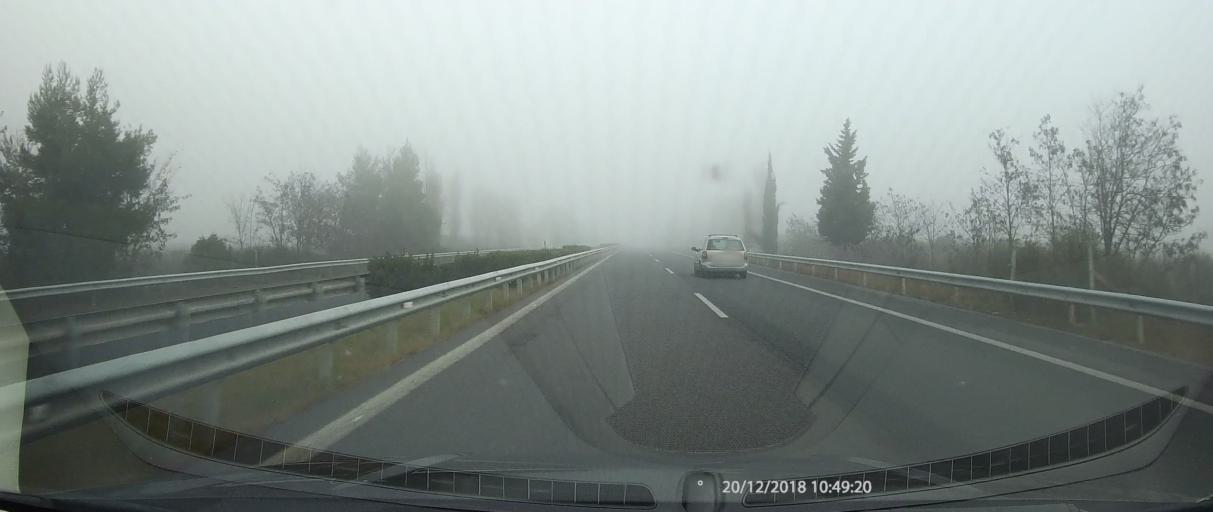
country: GR
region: Peloponnese
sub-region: Nomos Arkadias
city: Tripoli
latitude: 37.5371
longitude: 22.4140
